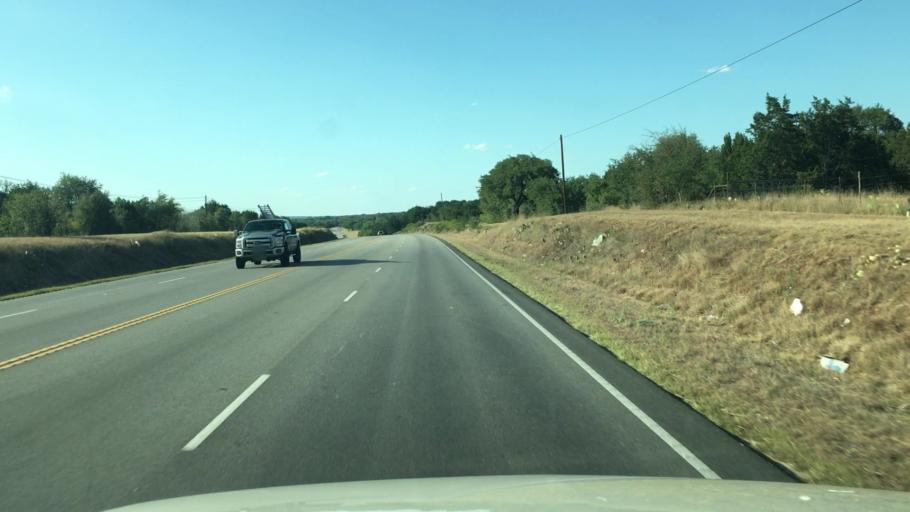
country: US
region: Texas
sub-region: Burnet County
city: Burnet
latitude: 30.6784
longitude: -98.2548
